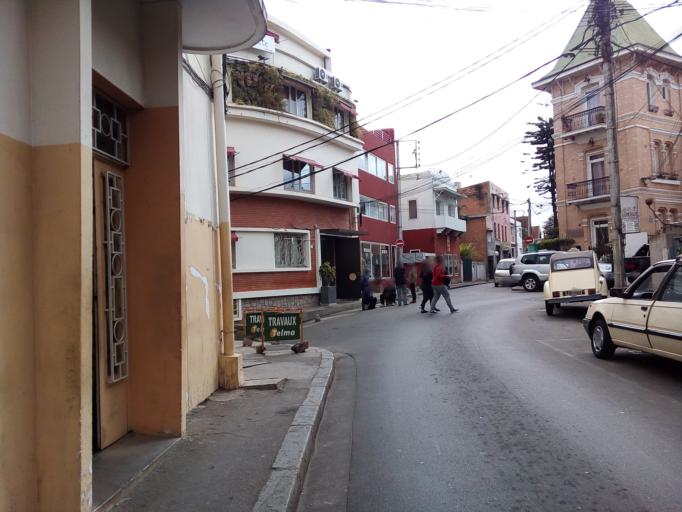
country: MG
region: Analamanga
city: Antananarivo
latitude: -18.9121
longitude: 47.5209
